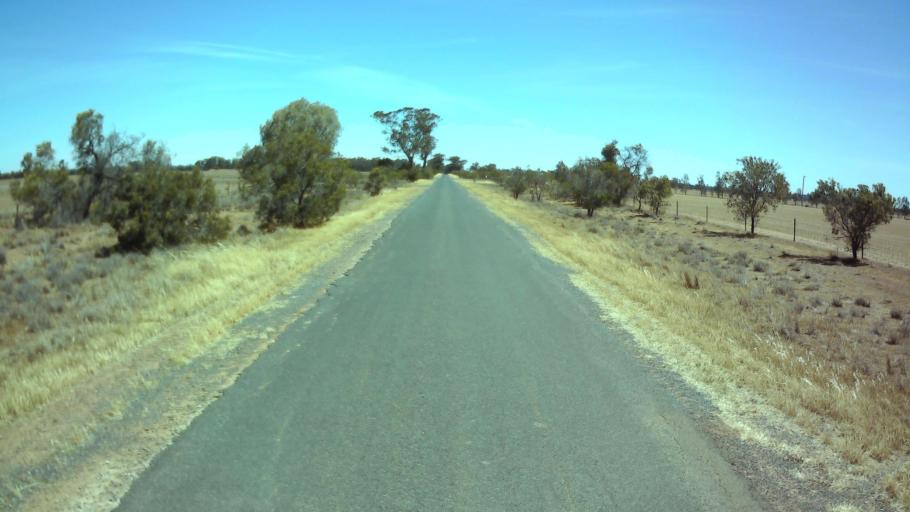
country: AU
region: New South Wales
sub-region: Weddin
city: Grenfell
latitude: -33.8938
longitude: 147.6877
